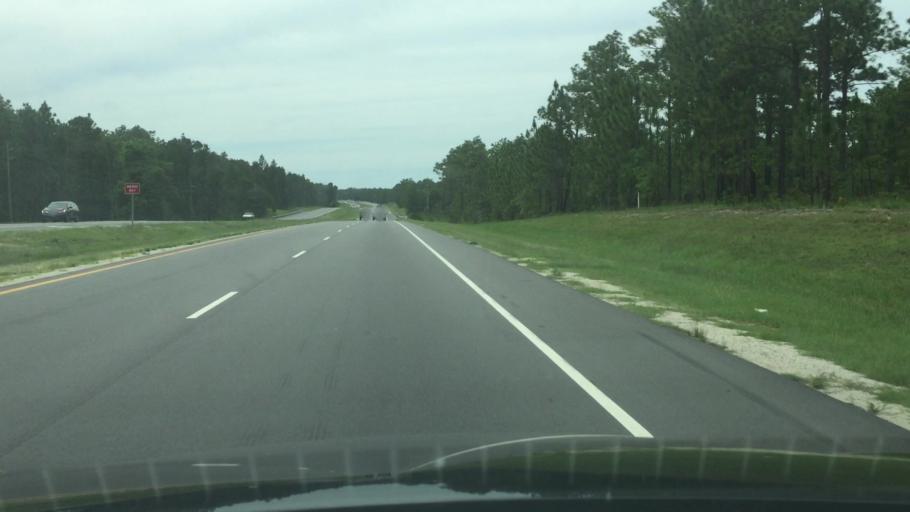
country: US
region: North Carolina
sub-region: Cumberland County
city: Spring Lake
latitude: 35.2202
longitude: -79.0039
